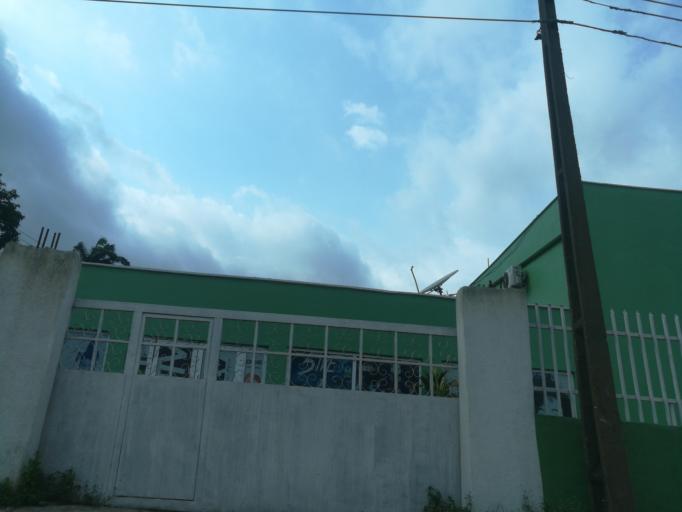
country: NG
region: Lagos
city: Oshodi
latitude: 6.5722
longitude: 3.3577
